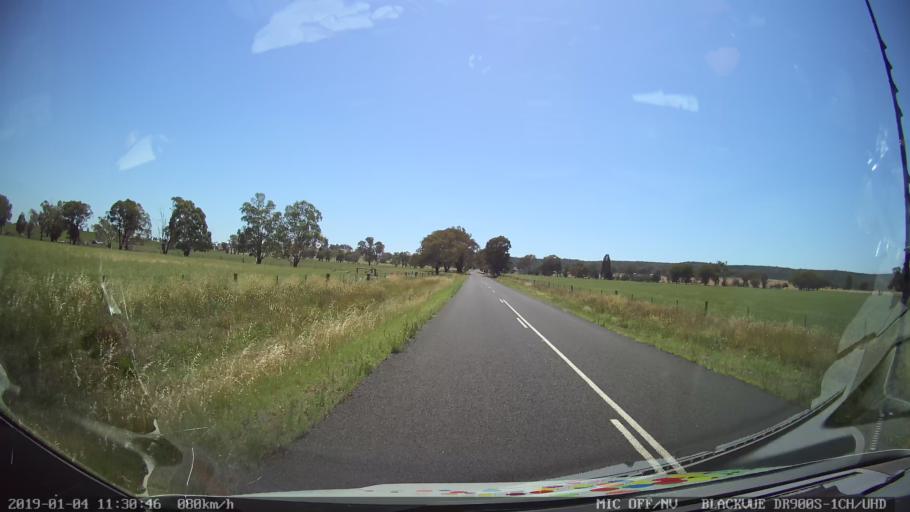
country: AU
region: New South Wales
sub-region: Cabonne
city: Molong
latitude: -33.0756
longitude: 148.7849
